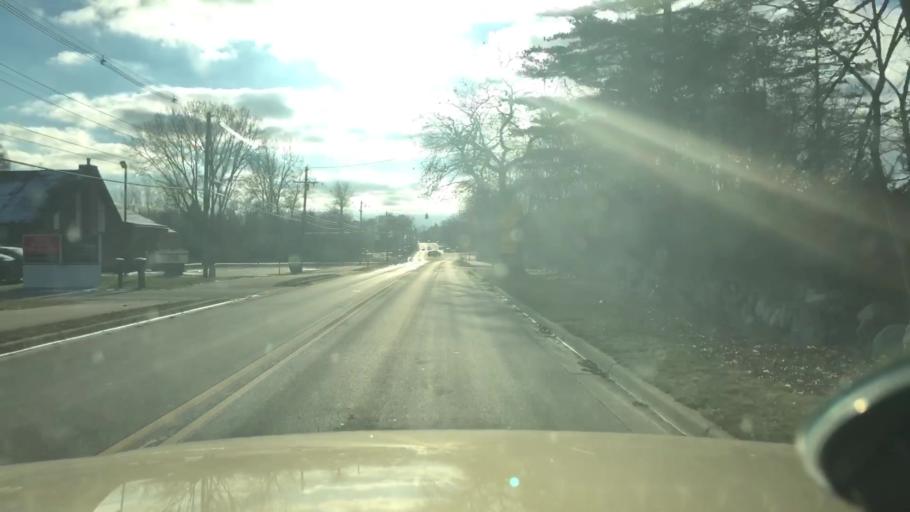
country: US
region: Michigan
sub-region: Jackson County
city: Vandercook Lake
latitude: 42.2061
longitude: -84.4312
